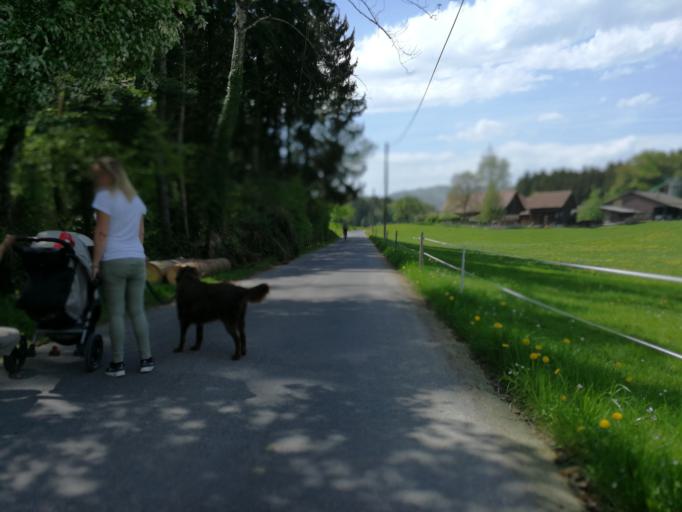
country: CH
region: Zurich
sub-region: Bezirk Hinwil
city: Binzikon
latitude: 47.2818
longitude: 8.7446
